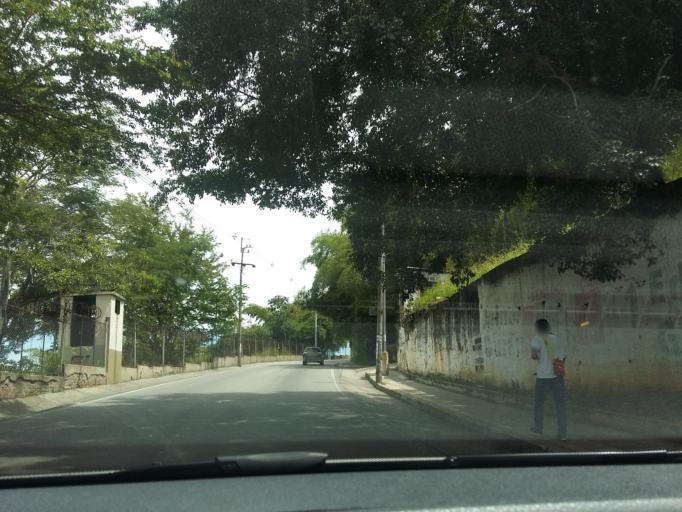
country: CO
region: Santander
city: Bucaramanga
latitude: 7.1320
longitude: -73.1079
